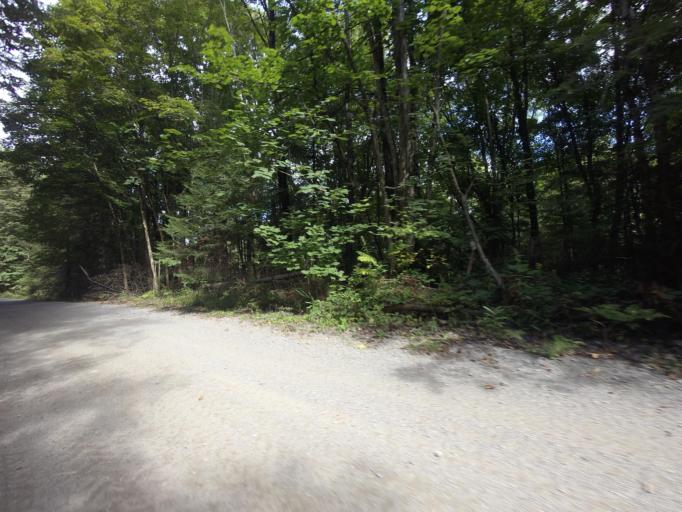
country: CA
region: Ontario
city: Omemee
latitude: 44.7520
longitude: -78.6702
